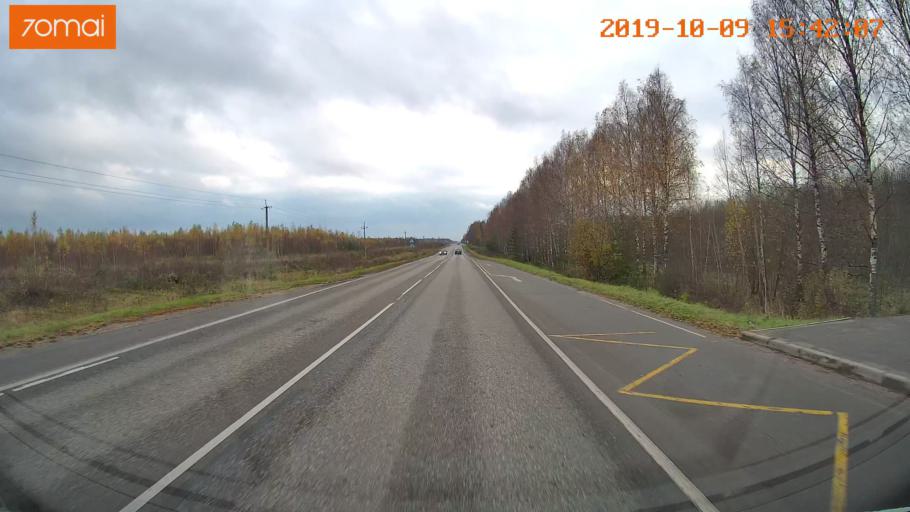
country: RU
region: Kostroma
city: Oktyabr'skiy
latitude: 57.8717
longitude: 41.1126
